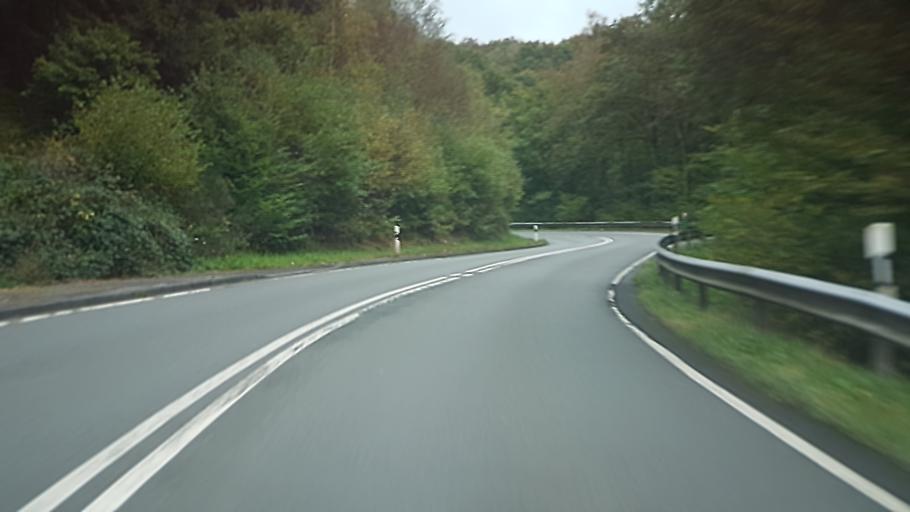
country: DE
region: North Rhine-Westphalia
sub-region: Regierungsbezirk Arnsberg
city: Attendorn
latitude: 51.1480
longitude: 7.8564
